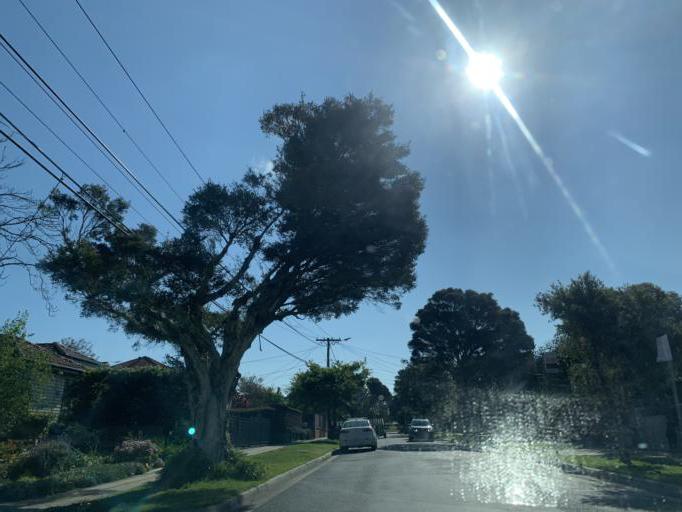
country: AU
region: Victoria
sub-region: Kingston
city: Mordialloc
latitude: -37.9916
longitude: 145.0876
